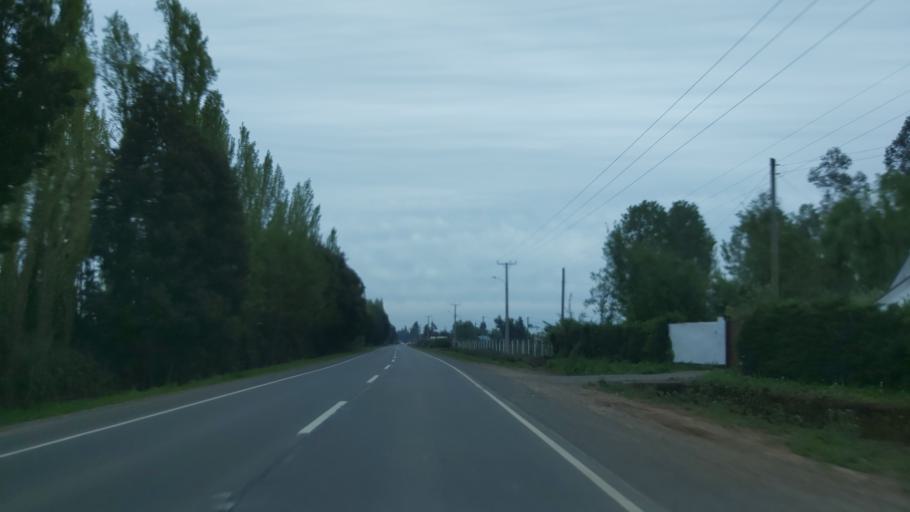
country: CL
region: Maule
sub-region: Provincia de Linares
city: Colbun
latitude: -35.7295
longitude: -71.4875
